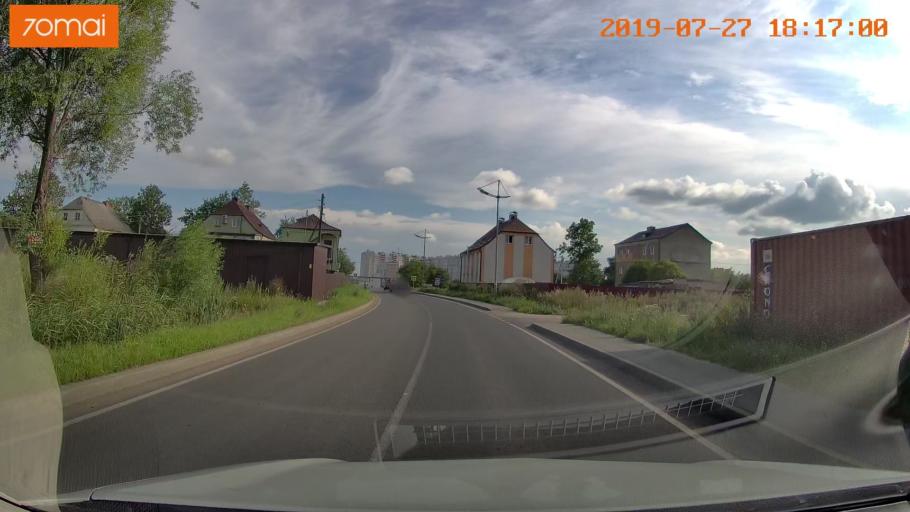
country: RU
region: Kaliningrad
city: Bol'shoe Isakovo
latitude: 54.7186
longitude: 20.5954
